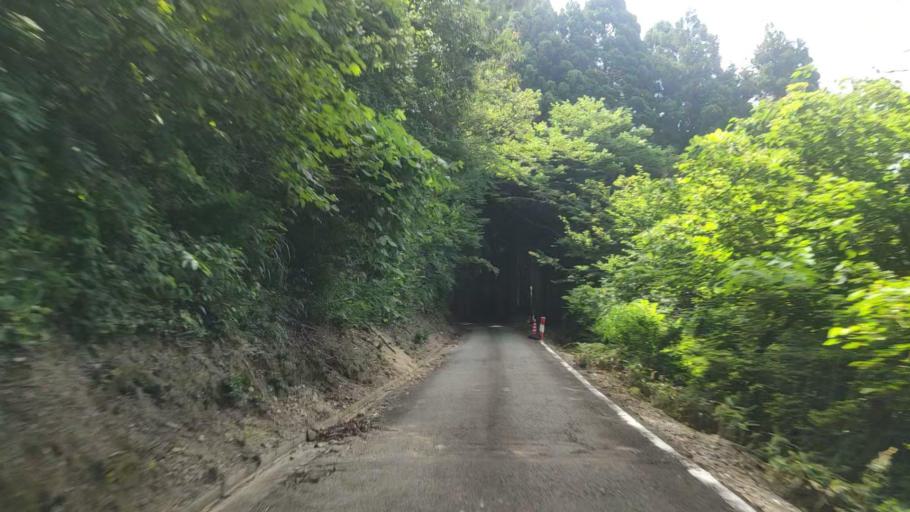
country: JP
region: Ishikawa
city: Komatsu
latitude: 36.2772
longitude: 136.5339
